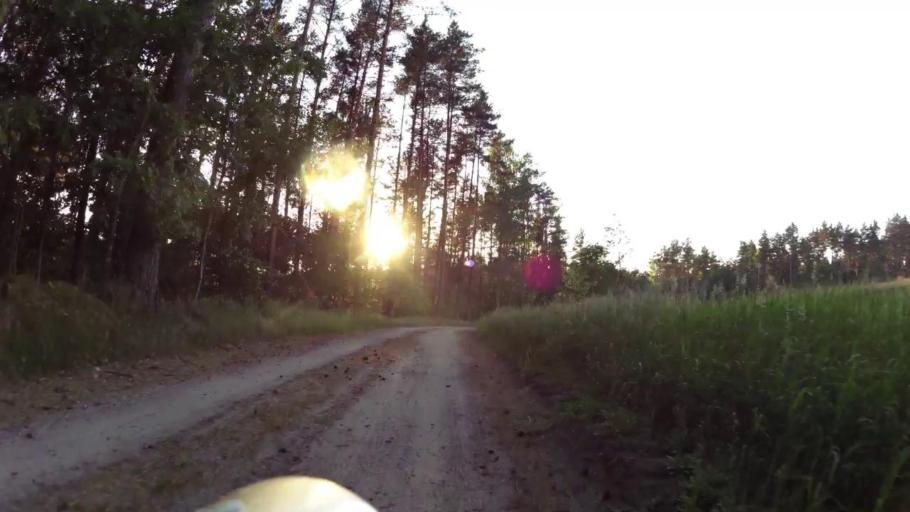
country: PL
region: West Pomeranian Voivodeship
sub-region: Powiat szczecinecki
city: Szczecinek
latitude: 53.8254
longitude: 16.6914
